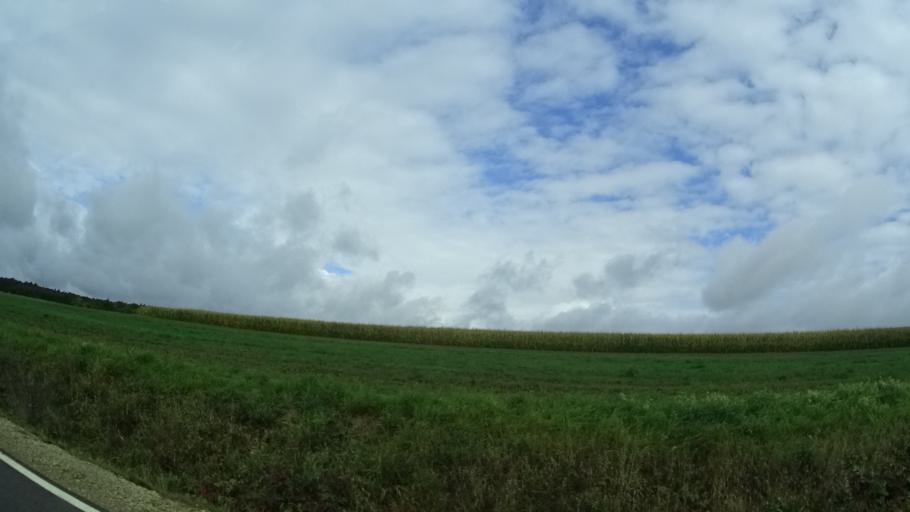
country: DE
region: Bavaria
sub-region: Upper Franconia
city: Zapfendorf
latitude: 50.0137
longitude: 10.9851
